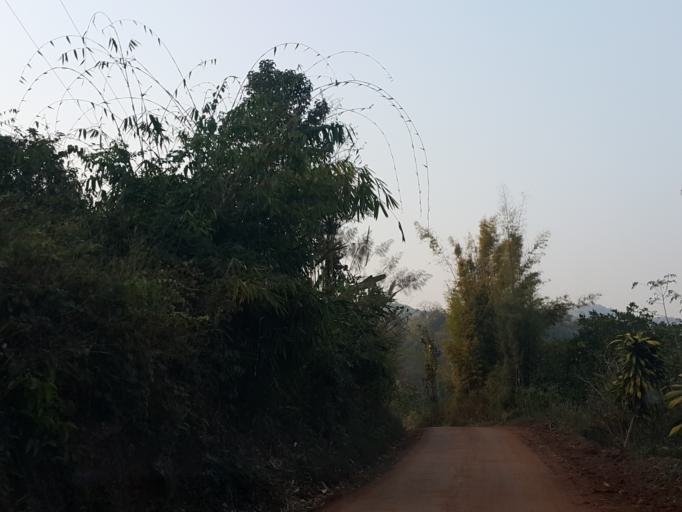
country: TH
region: Chiang Mai
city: Mae Taeng
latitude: 19.0733
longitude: 98.7713
